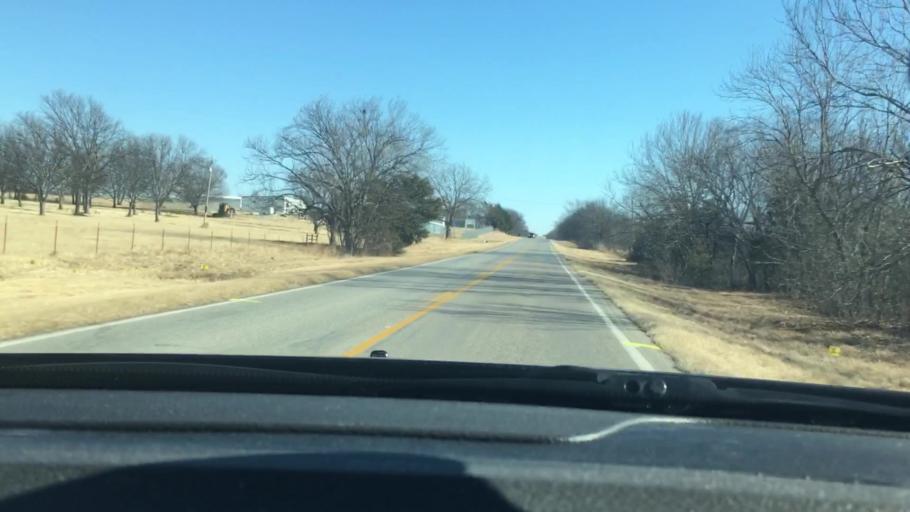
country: US
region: Oklahoma
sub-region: Garvin County
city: Wynnewood
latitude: 34.6515
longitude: -97.1250
